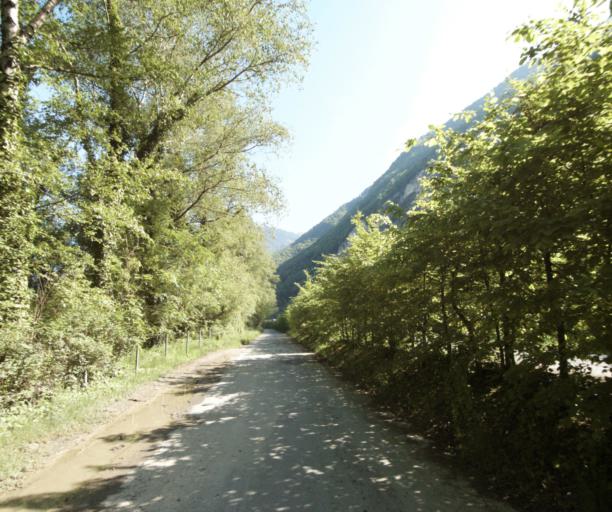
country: CH
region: Vaud
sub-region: Aigle District
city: Villeneuve
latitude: 46.3835
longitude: 6.9360
